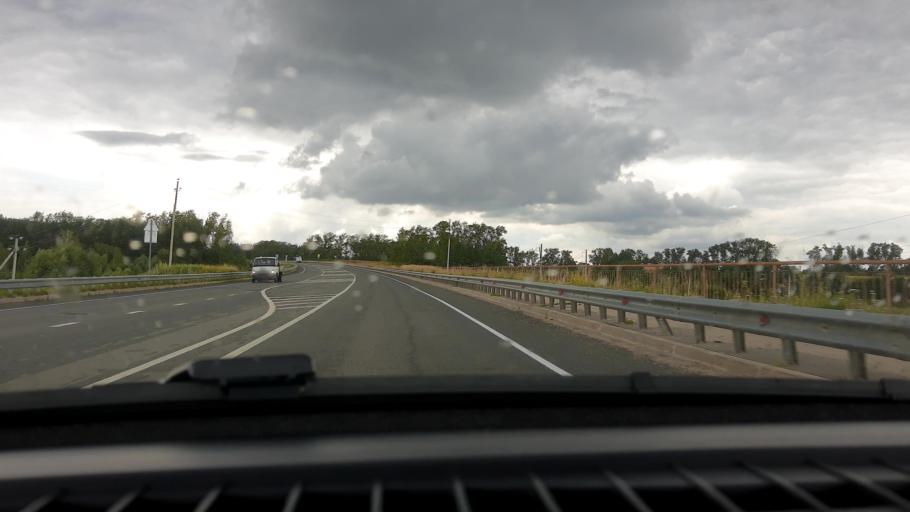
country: RU
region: Nizjnij Novgorod
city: Bol'shoye Murashkino
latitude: 55.8830
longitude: 44.7481
